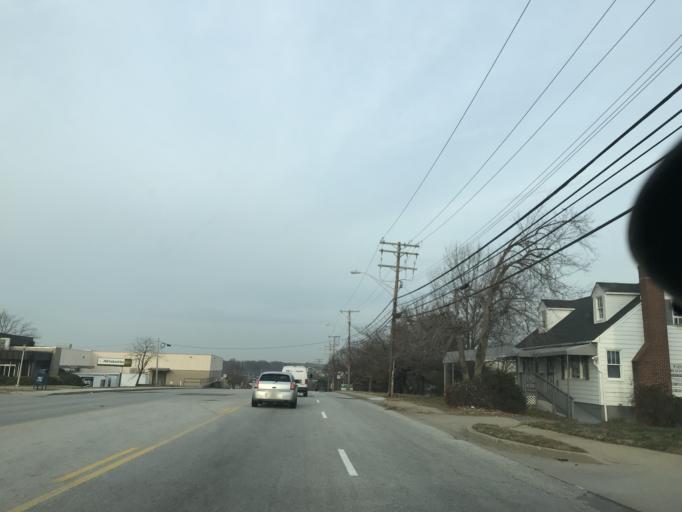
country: US
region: Maryland
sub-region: Prince George's County
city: Glenarden
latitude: 38.9405
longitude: -76.8628
